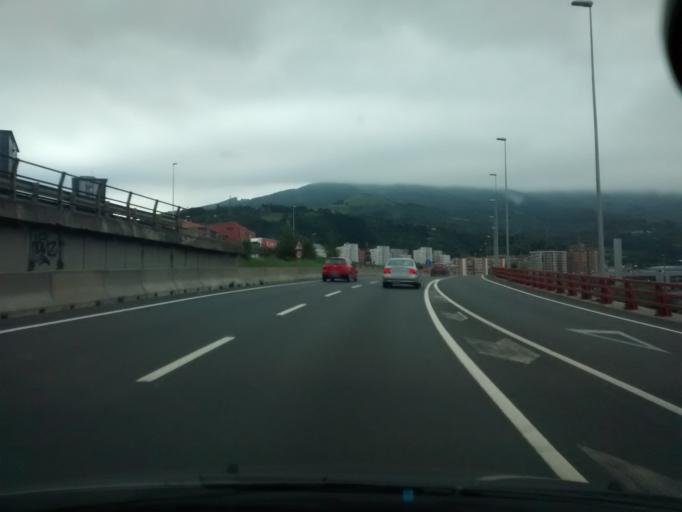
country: ES
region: Basque Country
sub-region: Bizkaia
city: Barakaldo
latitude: 43.2856
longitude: -2.9880
